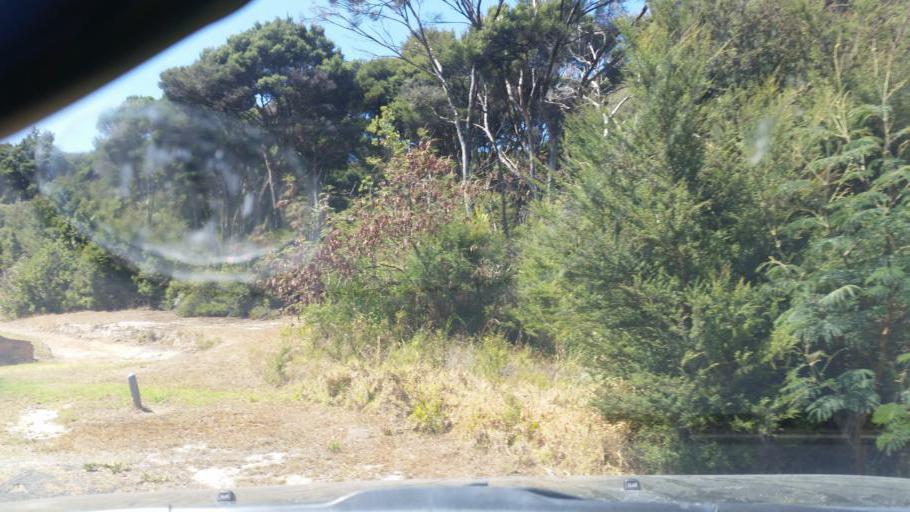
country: NZ
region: Northland
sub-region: Kaipara District
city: Dargaville
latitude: -36.2504
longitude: 174.1010
